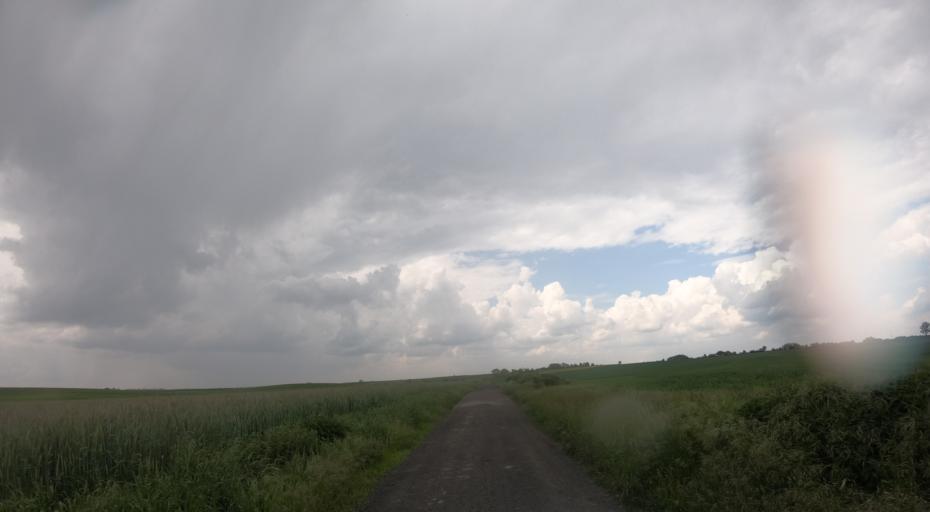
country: PL
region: West Pomeranian Voivodeship
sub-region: Powiat pyrzycki
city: Bielice
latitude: 53.2415
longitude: 14.7234
